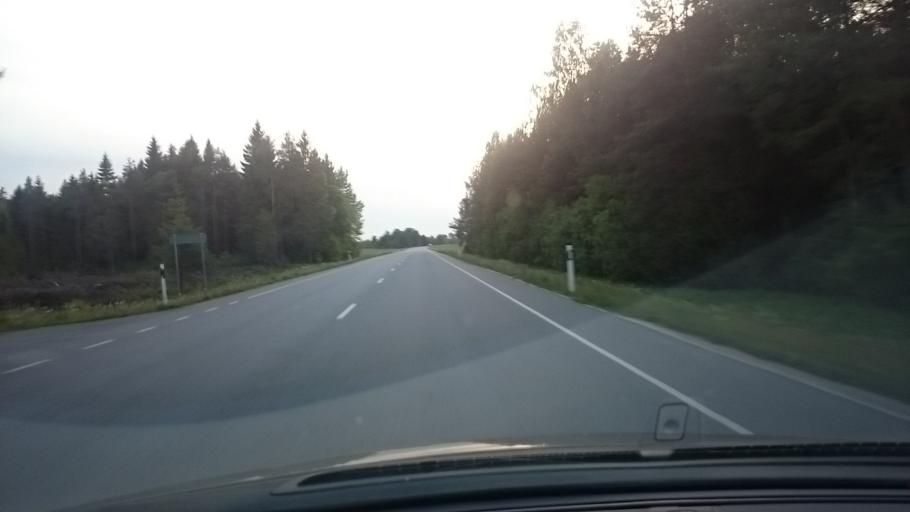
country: EE
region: Jaervamaa
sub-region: Tueri vald
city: Sarevere
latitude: 58.7656
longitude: 25.5364
